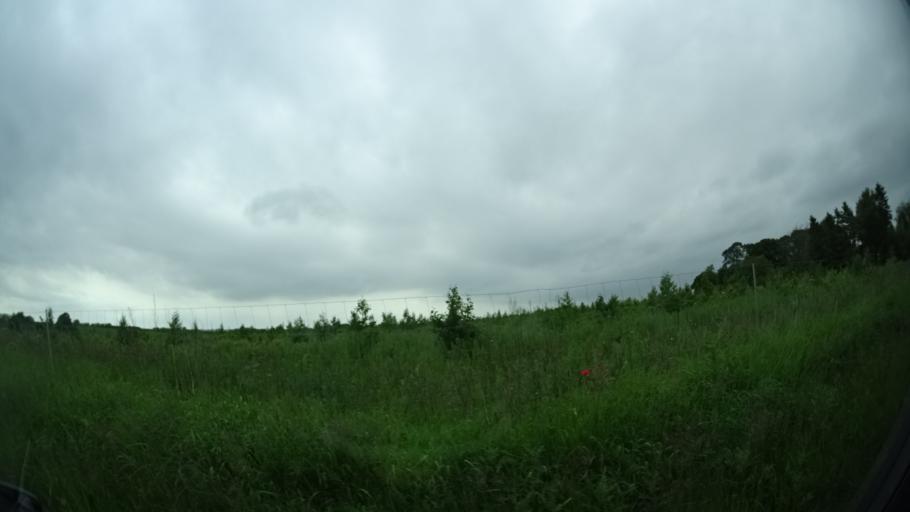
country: DK
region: Central Jutland
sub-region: Arhus Kommune
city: Solbjerg
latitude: 56.0583
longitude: 10.1028
